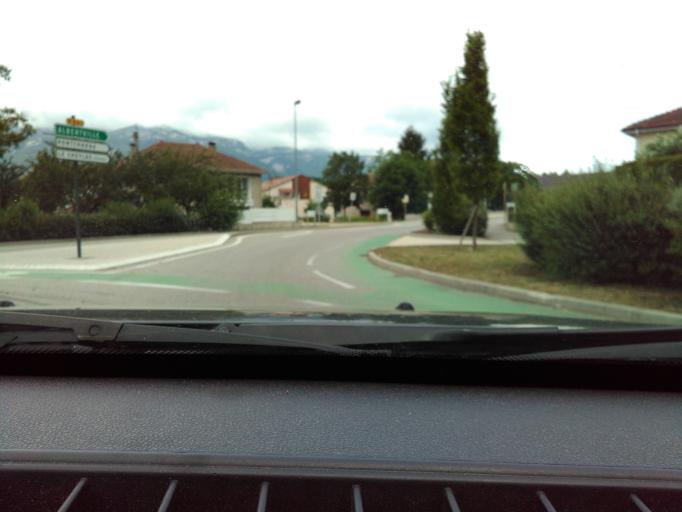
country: FR
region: Rhone-Alpes
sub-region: Departement de l'Isere
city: Le Cheylas
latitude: 45.3665
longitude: 5.9886
